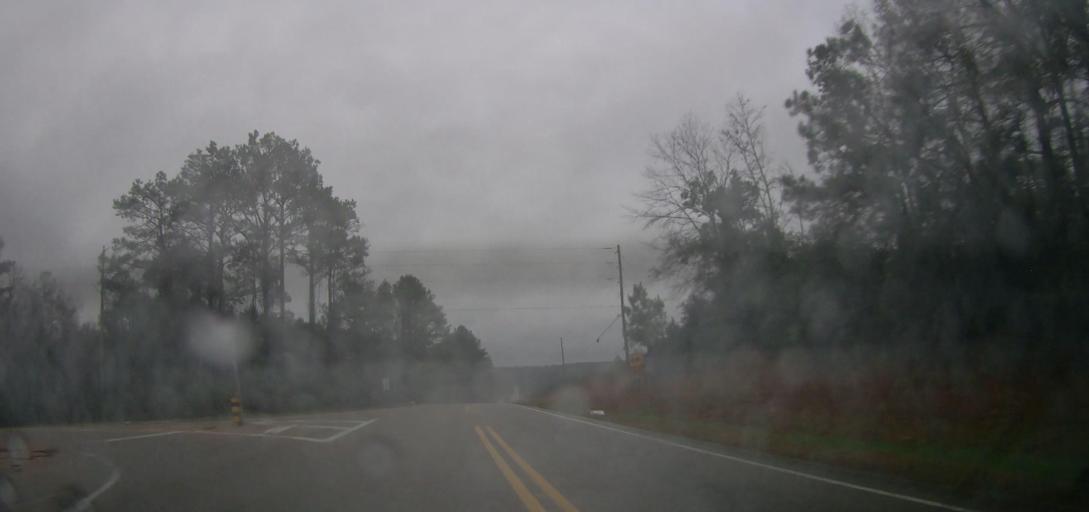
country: US
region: Alabama
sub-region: Autauga County
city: Pine Level
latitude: 32.5466
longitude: -86.6471
